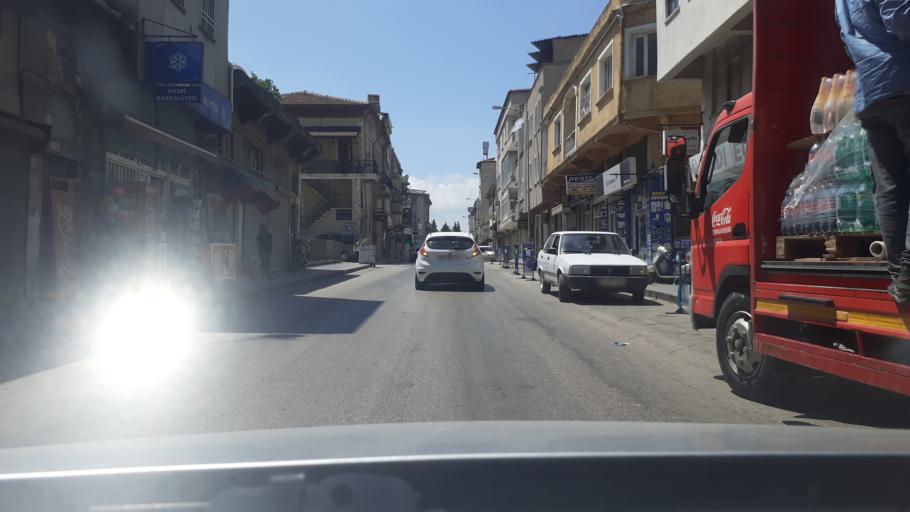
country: TR
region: Hatay
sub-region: Antakya Ilcesi
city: Antakya
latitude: 36.1982
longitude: 36.1625
